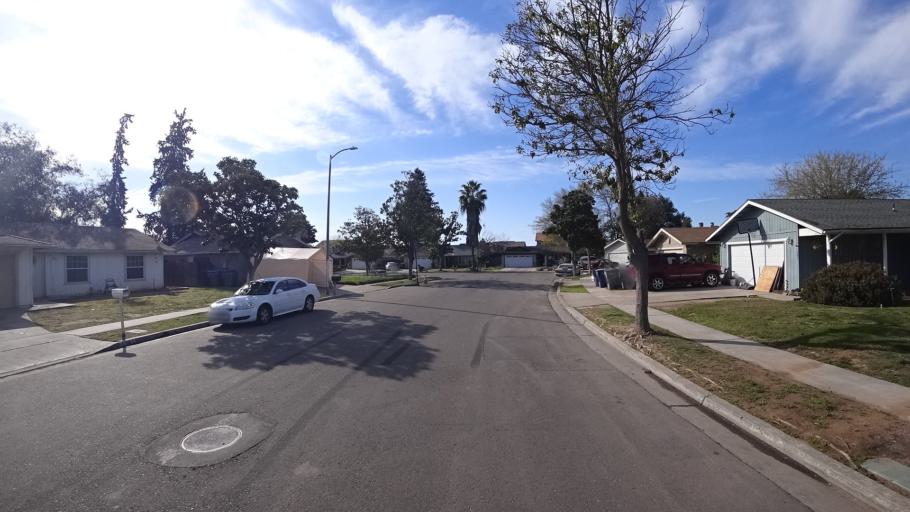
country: US
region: California
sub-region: Fresno County
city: West Park
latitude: 36.8053
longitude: -119.8870
